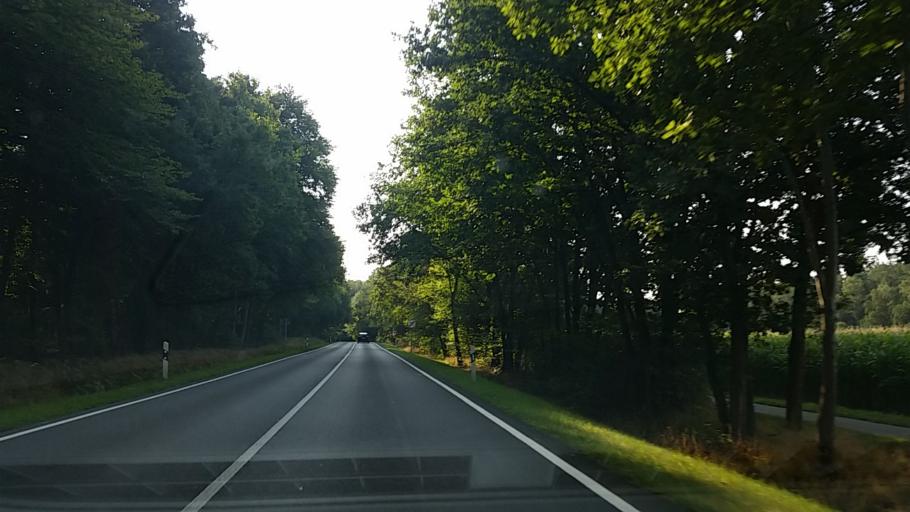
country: DE
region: Mecklenburg-Vorpommern
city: Wittenburg
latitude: 53.4885
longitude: 11.1036
